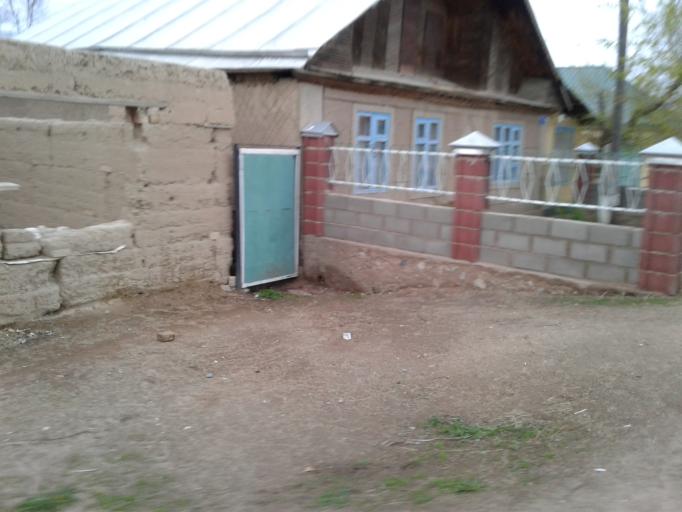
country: KG
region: Ysyk-Koel
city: Bokombayevskoye
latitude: 42.1155
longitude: 76.9857
